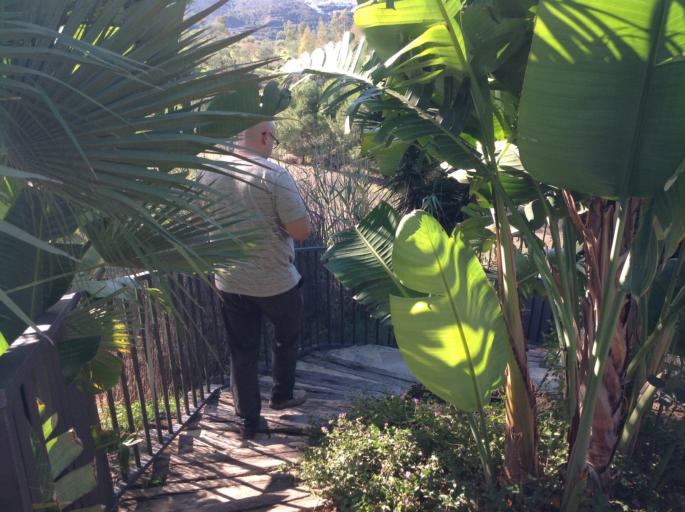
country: ES
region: Andalusia
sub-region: Provincia de Malaga
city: Vinuela
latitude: 36.8753
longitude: -4.1592
